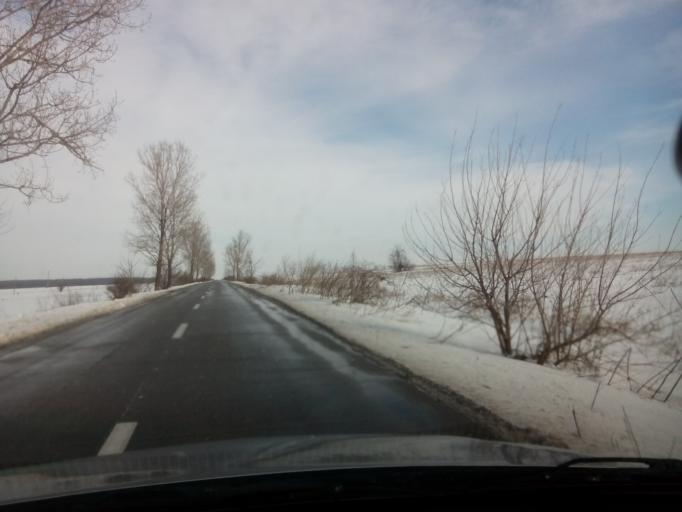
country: RO
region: Calarasi
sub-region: Comuna Soldanu
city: Soldanu
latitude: 44.2204
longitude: 26.5434
